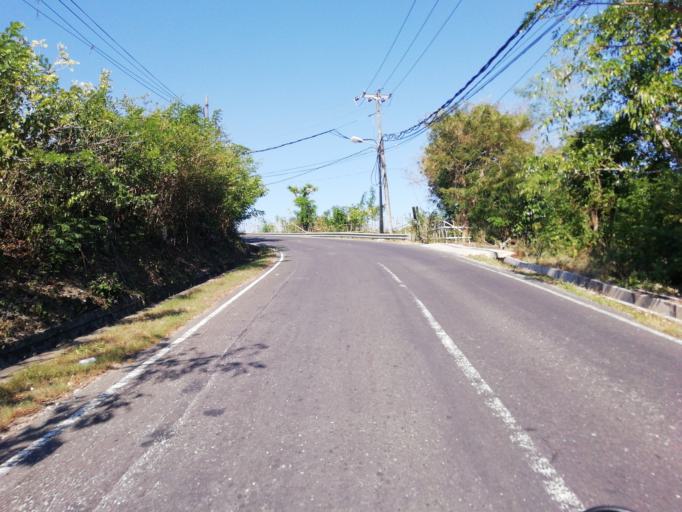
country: ID
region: Bali
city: Jimbaran
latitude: -8.8294
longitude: 115.1738
